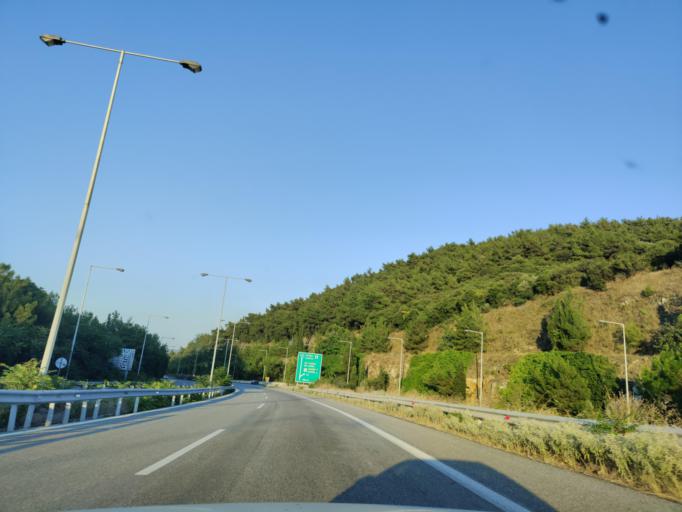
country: GR
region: East Macedonia and Thrace
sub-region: Nomos Kavalas
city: Kavala
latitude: 40.9528
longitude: 24.4550
